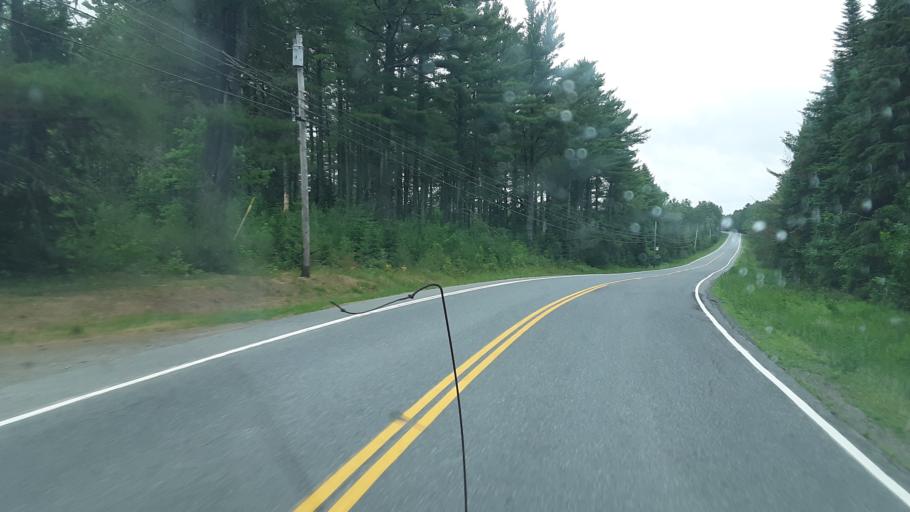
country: US
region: Maine
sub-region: Aroostook County
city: Presque Isle
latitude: 46.4779
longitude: -68.3876
